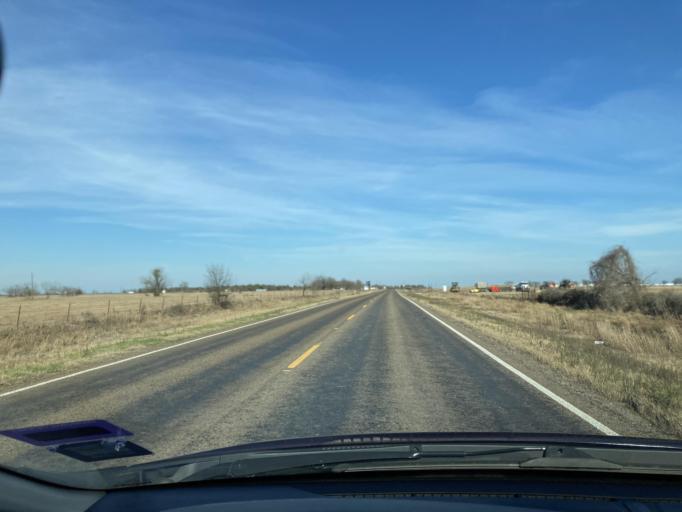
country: US
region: Texas
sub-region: Navarro County
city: Corsicana
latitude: 32.0312
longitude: -96.4074
